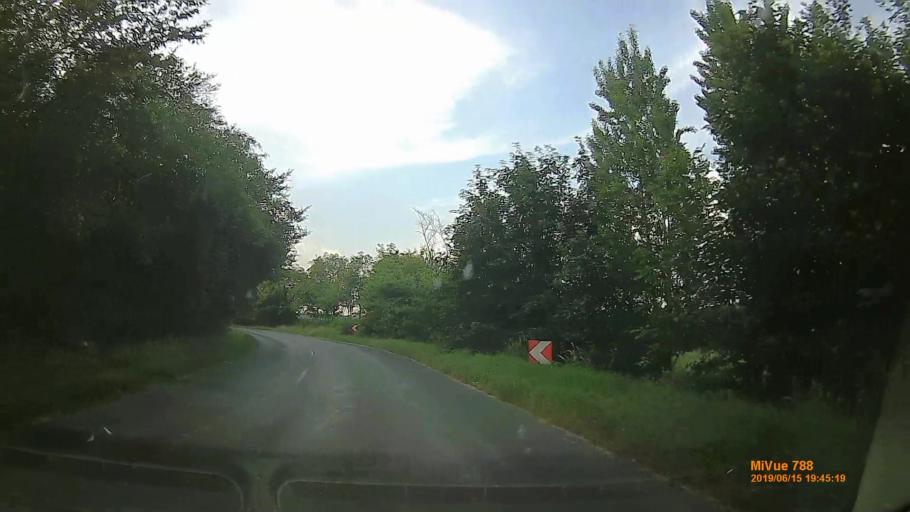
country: HU
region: Veszprem
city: Szentkiralyszabadja
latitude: 47.0084
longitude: 17.9655
